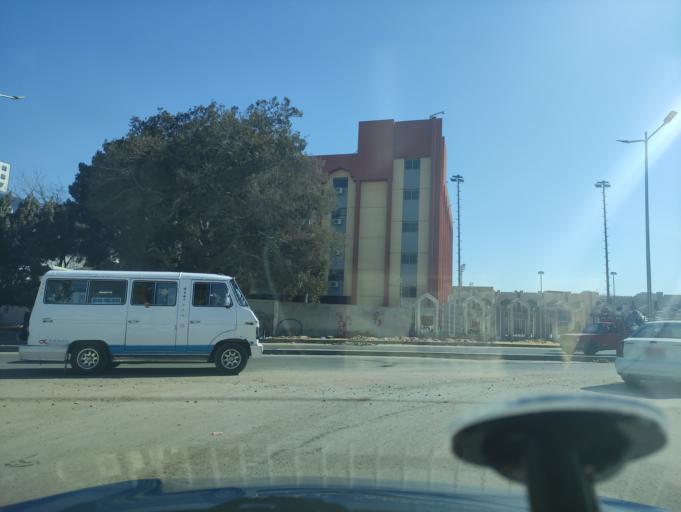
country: EG
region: Muhafazat al Qahirah
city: Cairo
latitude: 30.0585
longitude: 31.2770
